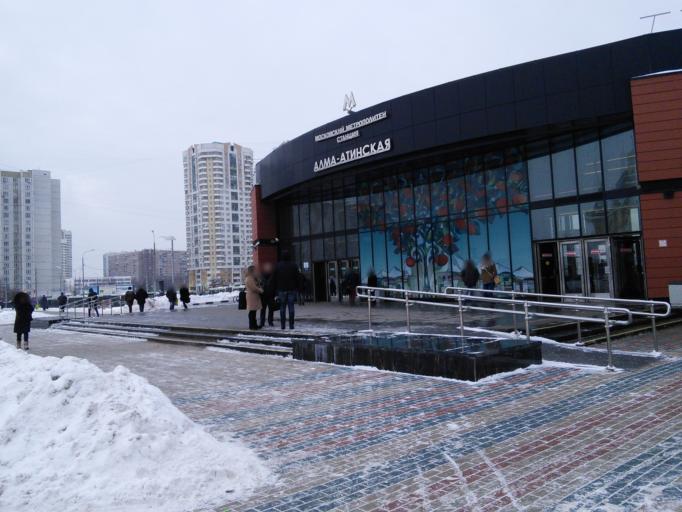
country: RU
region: Moscow
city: Brateyevo
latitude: 55.6334
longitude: 37.7657
